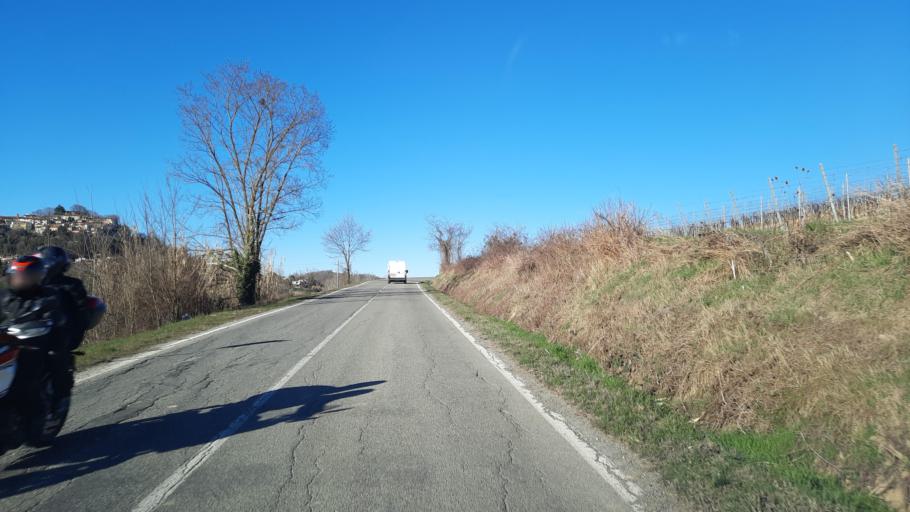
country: IT
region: Piedmont
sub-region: Provincia di Alessandria
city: Rosignano Monferrato
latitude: 45.0721
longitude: 8.4044
